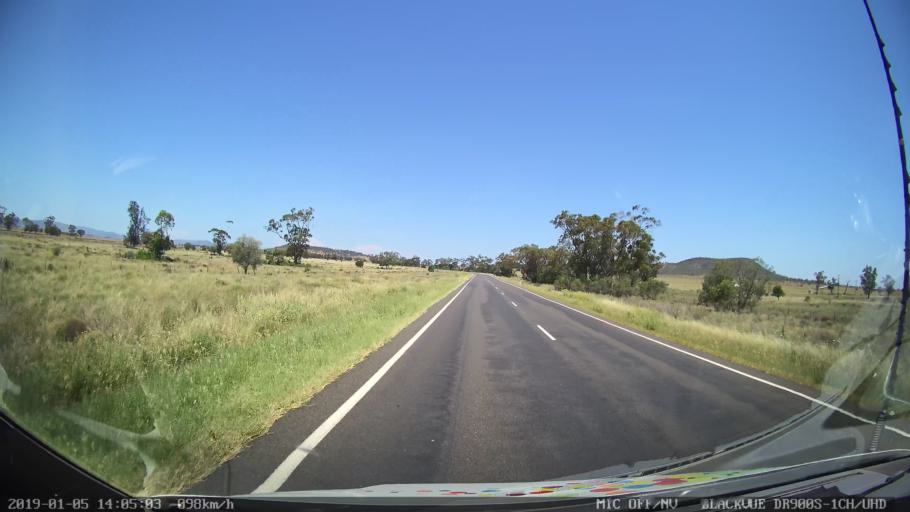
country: AU
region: New South Wales
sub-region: Gunnedah
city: Gunnedah
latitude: -31.2066
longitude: 150.3710
